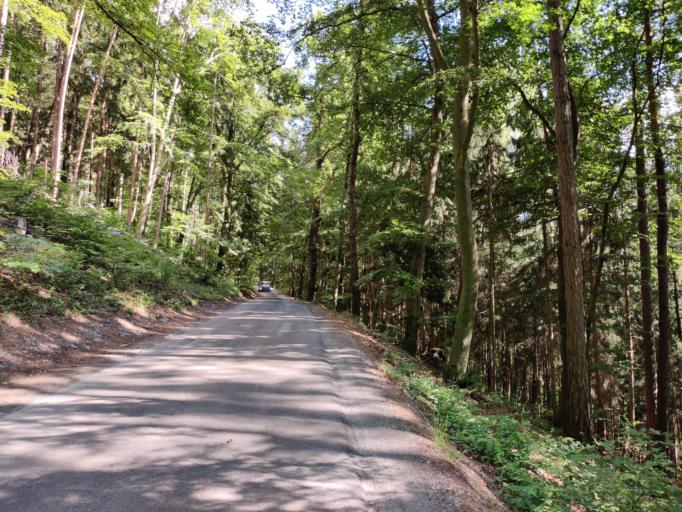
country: AT
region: Styria
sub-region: Graz Stadt
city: Wetzelsdorf
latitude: 47.0343
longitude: 15.3677
